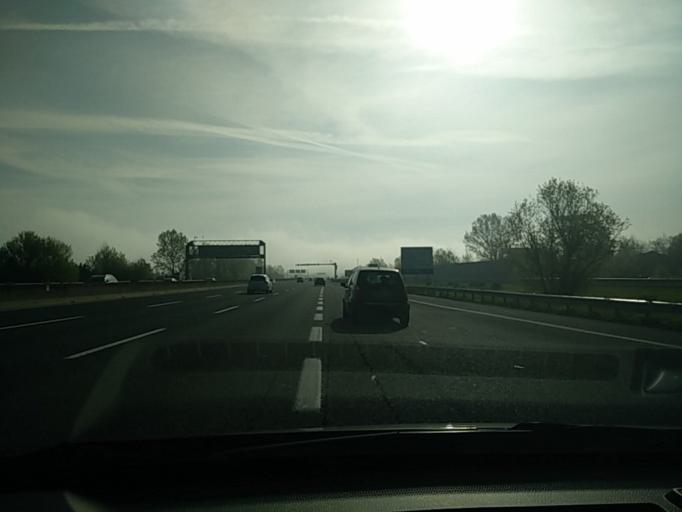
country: IT
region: Emilia-Romagna
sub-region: Provincia di Bologna
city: Villanova
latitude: 44.4805
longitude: 11.4336
